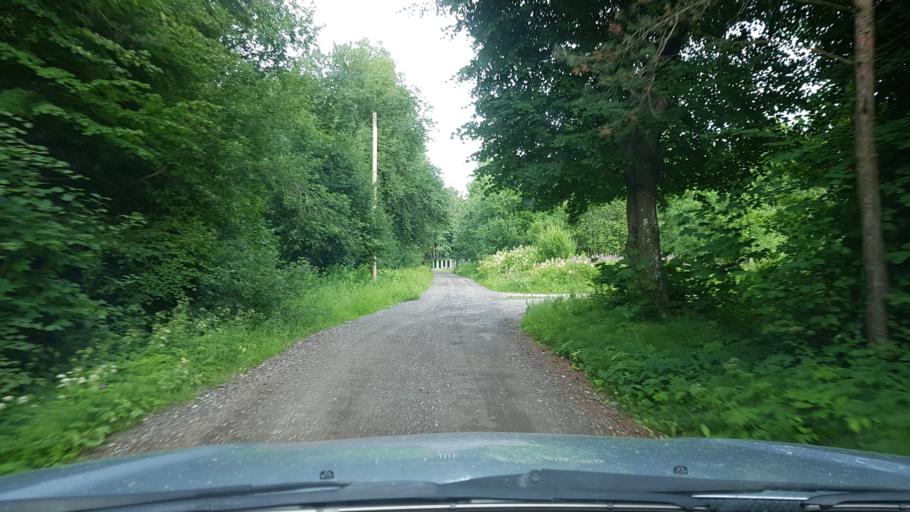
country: EE
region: Ida-Virumaa
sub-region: Narva-Joesuu linn
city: Narva-Joesuu
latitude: 59.4571
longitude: 28.0683
